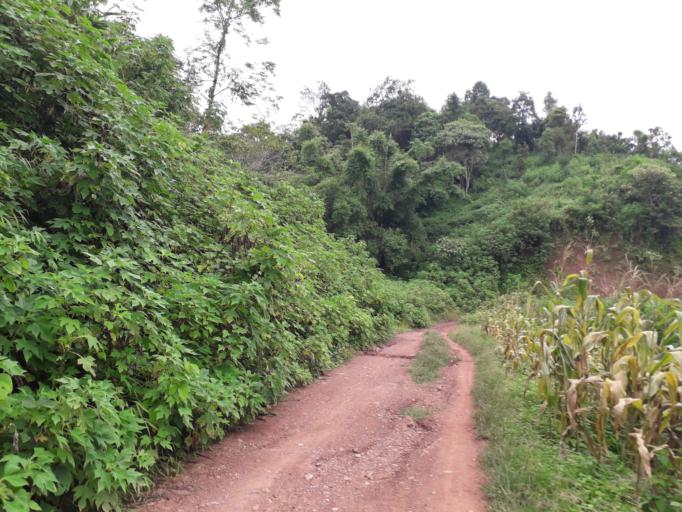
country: CN
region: Yunnan
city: Menglie
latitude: 22.2428
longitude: 101.6100
